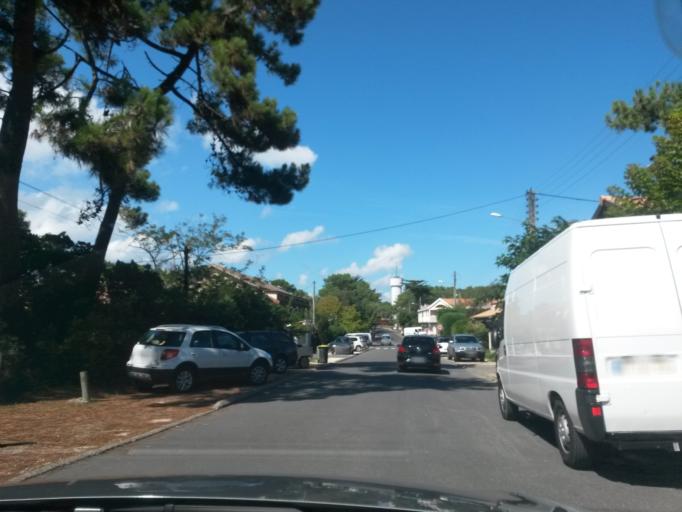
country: FR
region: Aquitaine
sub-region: Departement de la Gironde
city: Arcachon
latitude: 44.6473
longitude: -1.2489
